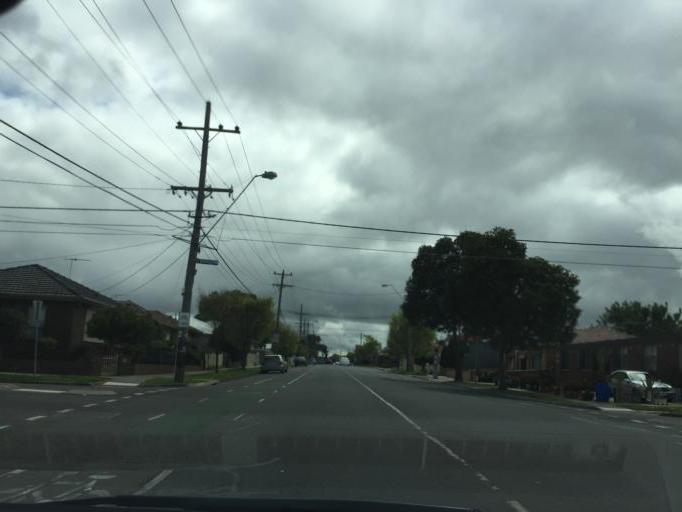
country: AU
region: Victoria
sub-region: Brimbank
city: Sunshine West
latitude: -37.7945
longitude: 144.8306
